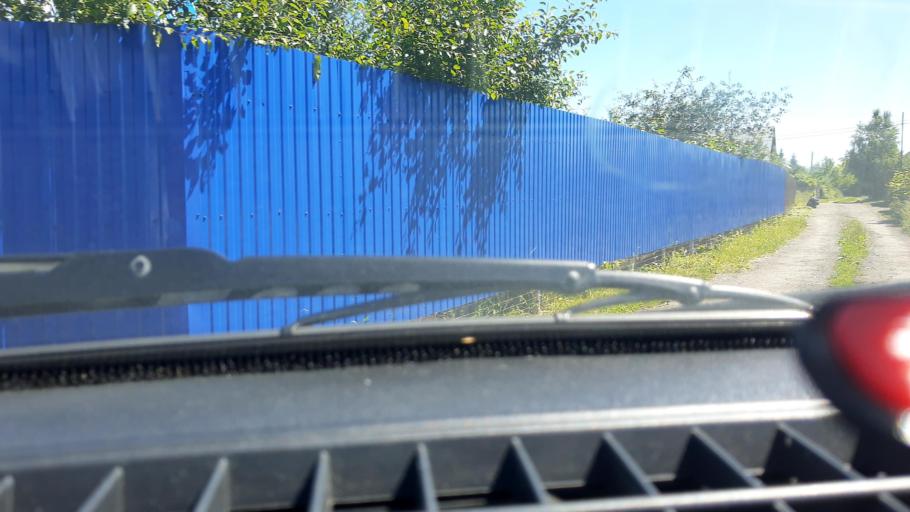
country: RU
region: Bashkortostan
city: Ufa
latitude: 54.5599
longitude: 55.9283
